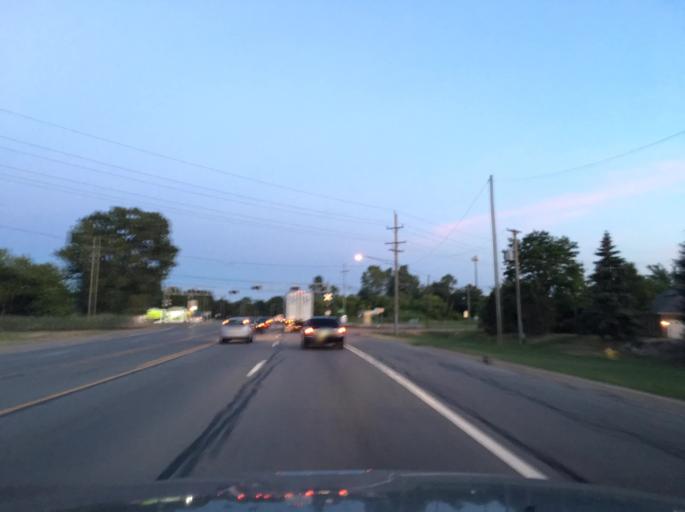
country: US
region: Michigan
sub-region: Macomb County
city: Clinton
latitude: 42.5860
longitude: -82.9033
